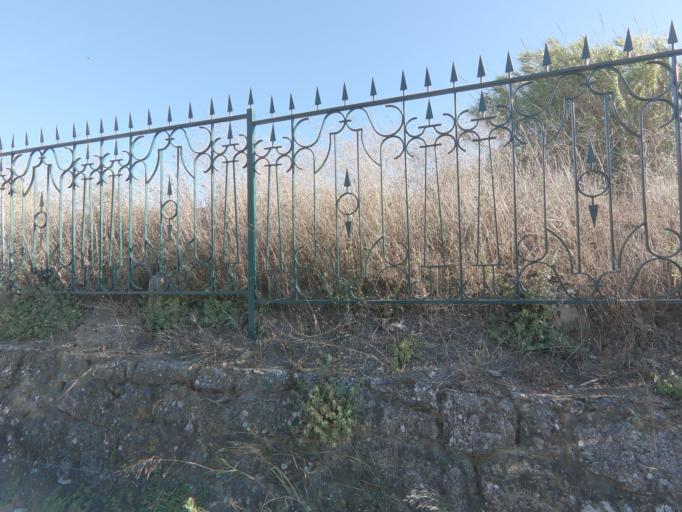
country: PT
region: Setubal
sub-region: Palmela
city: Quinta do Anjo
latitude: 38.5240
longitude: -8.9980
